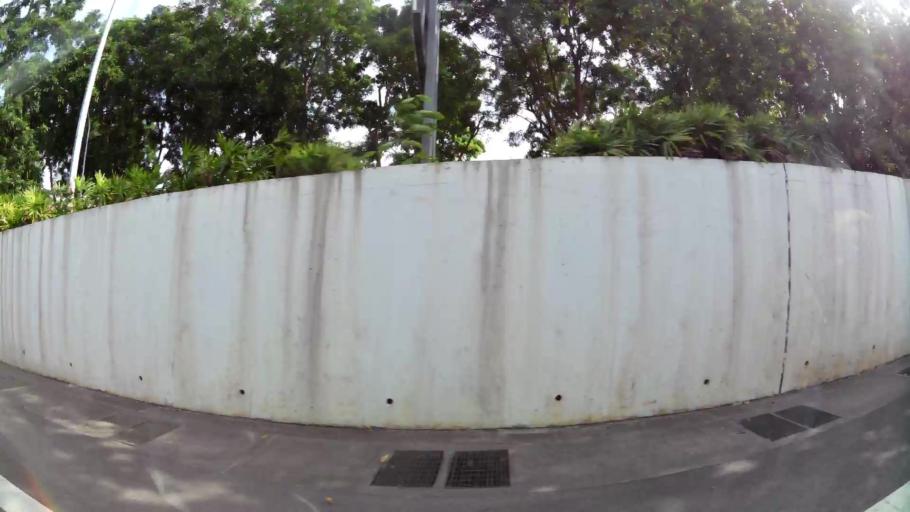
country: MY
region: Johor
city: Johor Bahru
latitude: 1.3404
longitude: 103.6453
